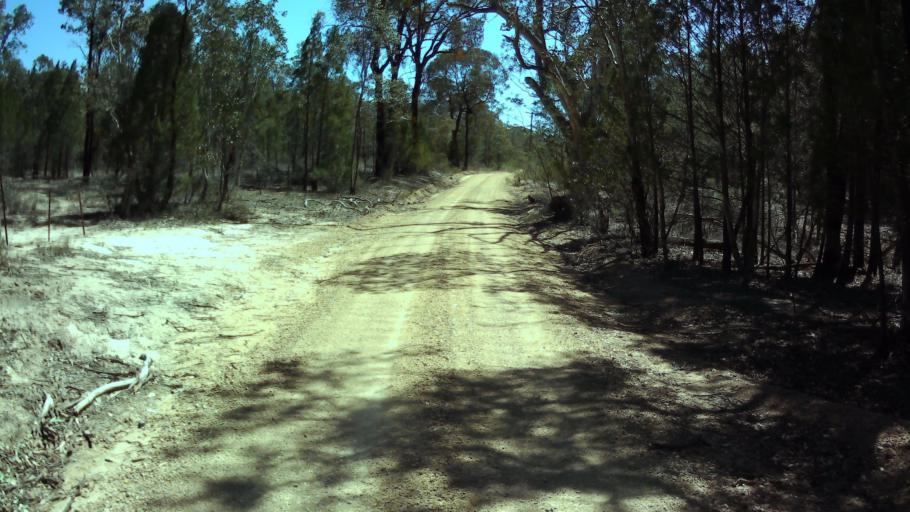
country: AU
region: New South Wales
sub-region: Cowra
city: Cowra
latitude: -33.8505
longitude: 148.4497
